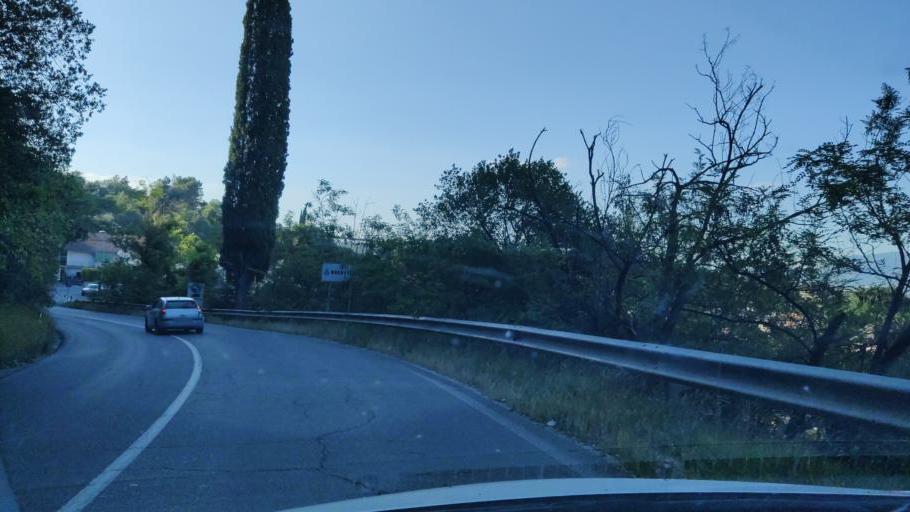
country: IT
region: Umbria
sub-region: Provincia di Terni
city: Narni Scalo
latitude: 42.5275
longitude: 12.5138
